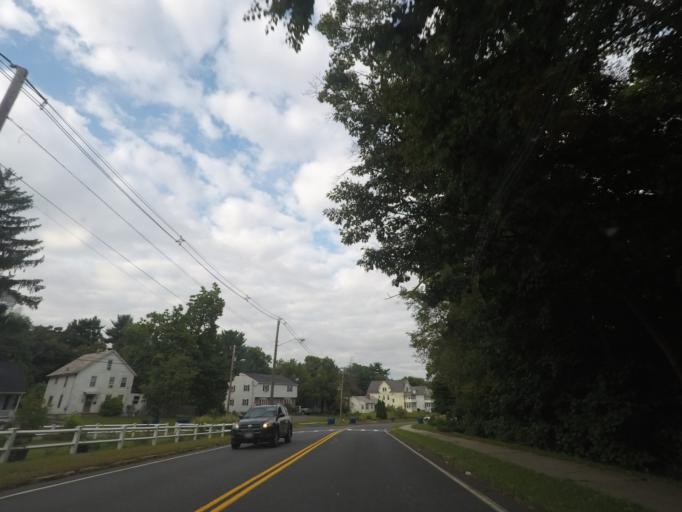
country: US
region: Massachusetts
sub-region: Hampden County
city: West Springfield
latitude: 42.1125
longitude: -72.6308
